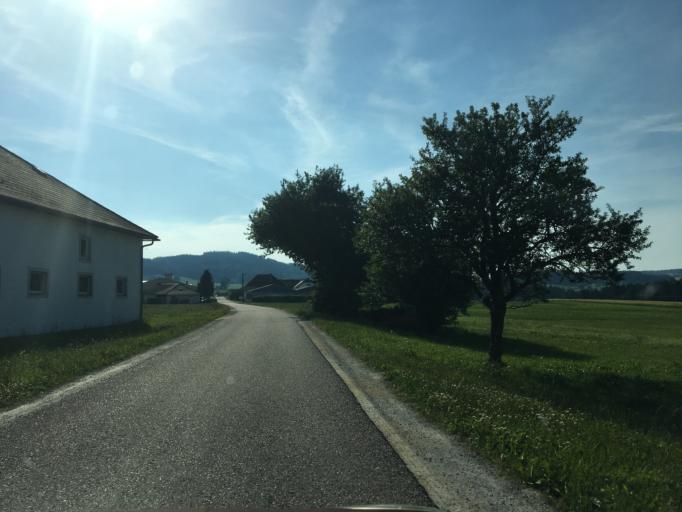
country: AT
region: Upper Austria
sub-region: Politischer Bezirk Urfahr-Umgebung
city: Oberneukirchen
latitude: 48.4952
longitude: 14.2288
